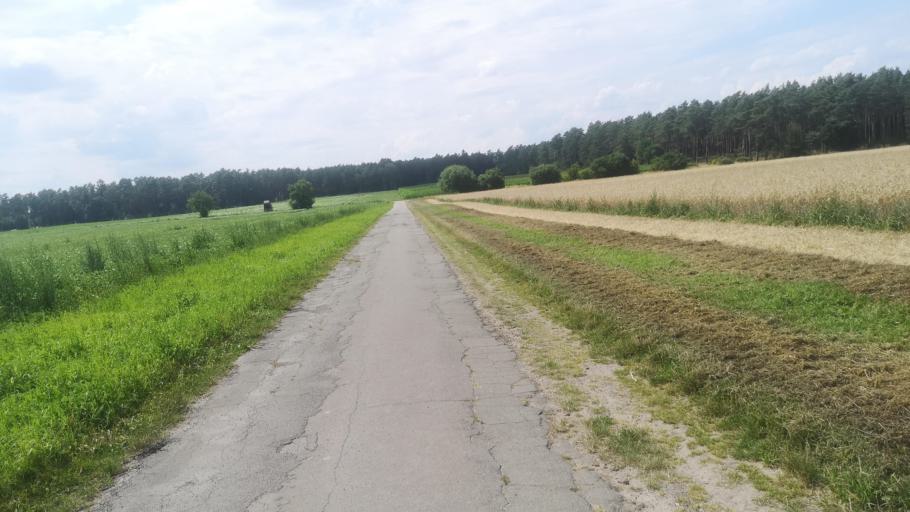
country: DE
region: Lower Saxony
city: Dahlem
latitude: 53.2336
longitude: 10.7352
